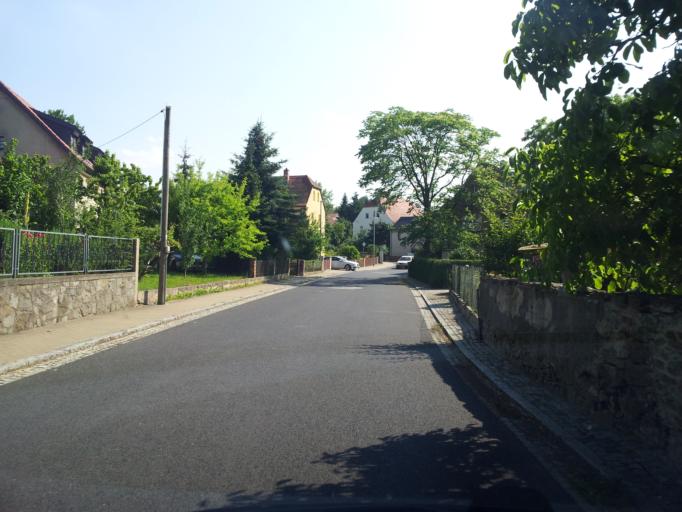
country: DE
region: Saxony
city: Wachau
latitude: 51.1621
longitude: 13.8774
